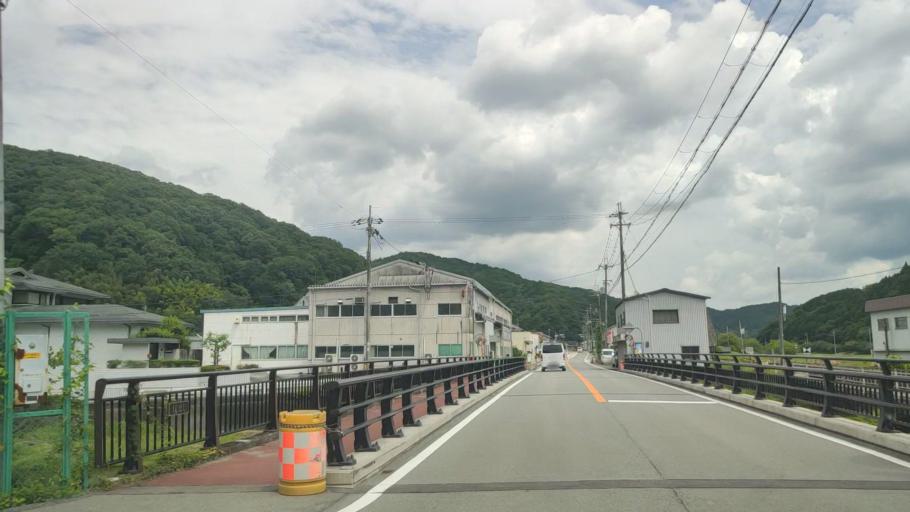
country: JP
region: Hyogo
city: Yamazakicho-nakabirose
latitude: 34.9863
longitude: 134.4335
